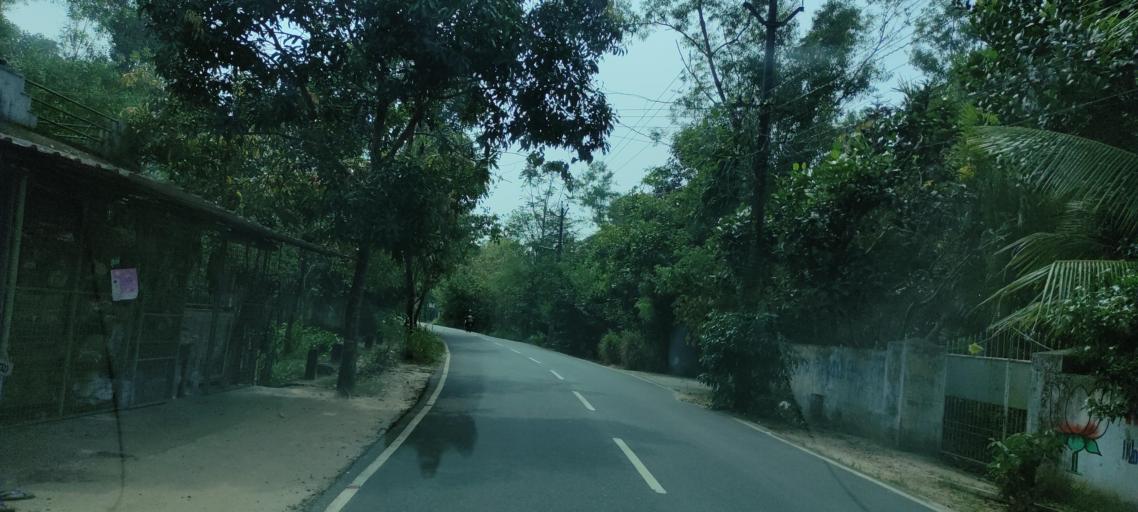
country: IN
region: Kerala
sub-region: Alappuzha
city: Alleppey
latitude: 9.5630
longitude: 76.3344
